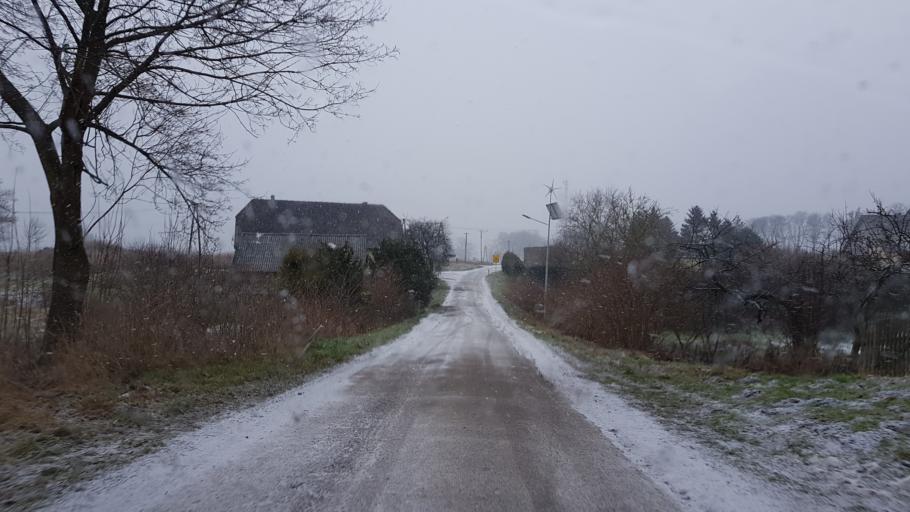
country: PL
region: West Pomeranian Voivodeship
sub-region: Powiat slawienski
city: Slawno
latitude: 54.2735
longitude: 16.6365
